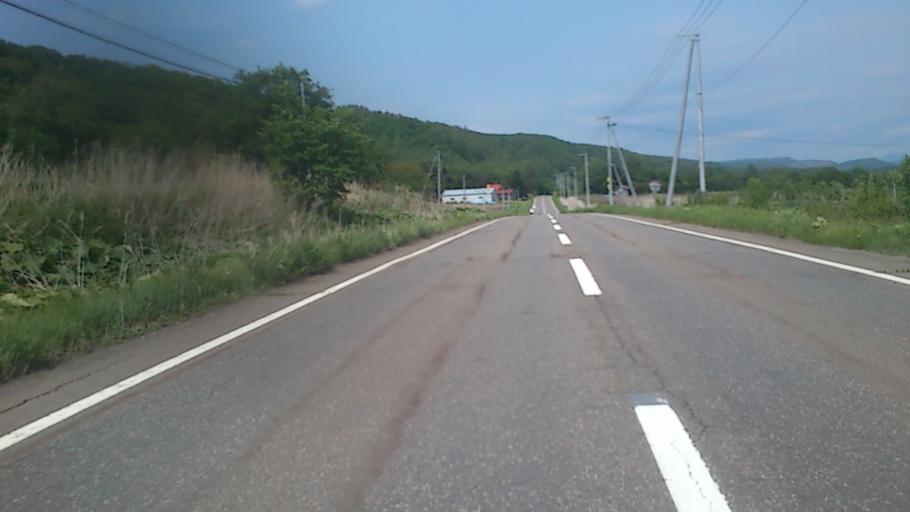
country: JP
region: Hokkaido
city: Otofuke
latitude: 43.2583
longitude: 143.5723
